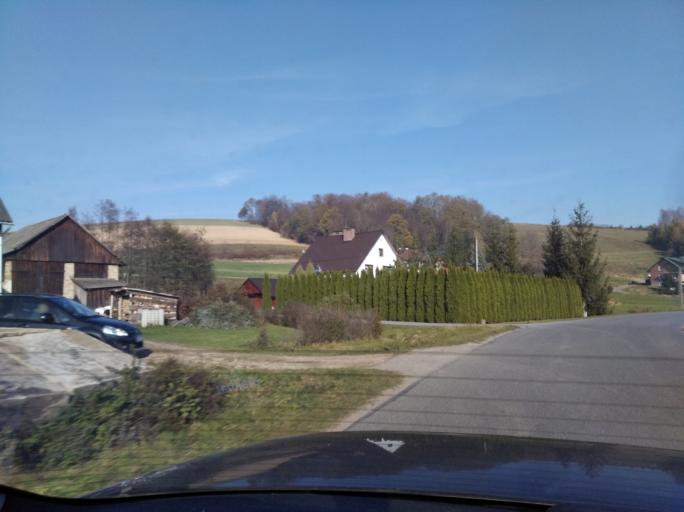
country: PL
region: Subcarpathian Voivodeship
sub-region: Powiat ropczycko-sedziszowski
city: Wielopole Skrzynskie
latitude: 49.9433
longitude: 21.5782
